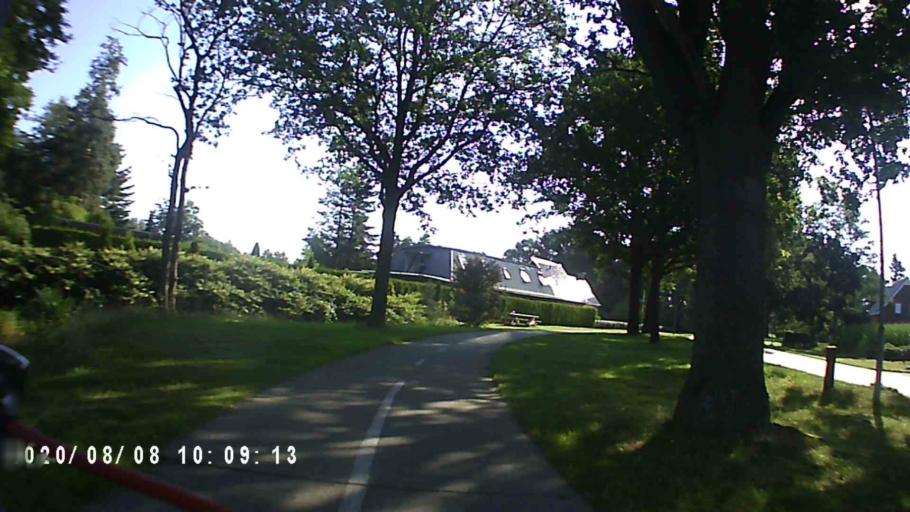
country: NL
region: Groningen
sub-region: Gemeente Leek
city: Leek
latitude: 53.1217
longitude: 6.3644
